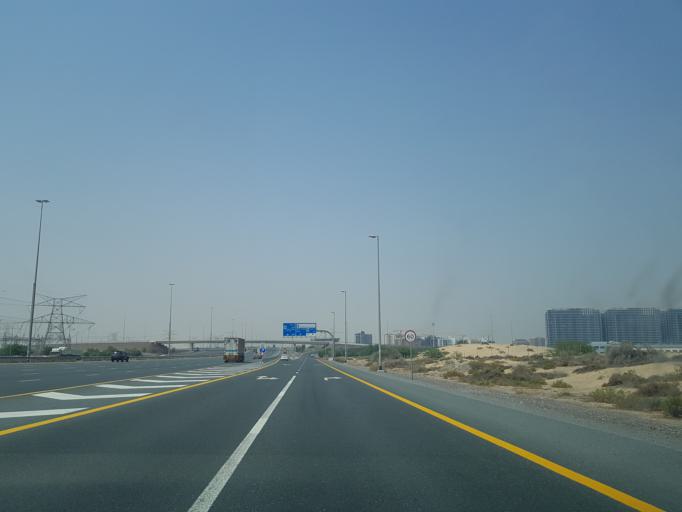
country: AE
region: Dubai
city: Dubai
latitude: 25.0918
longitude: 55.3981
